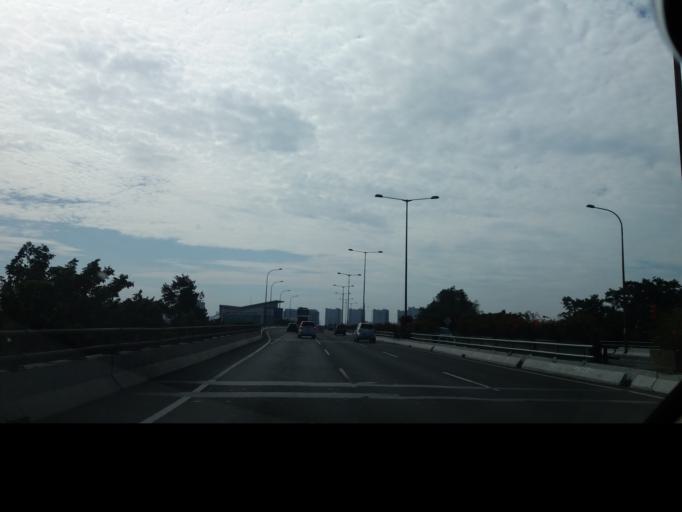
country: ID
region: Jakarta Raya
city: Jakarta
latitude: -6.2047
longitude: 106.8735
